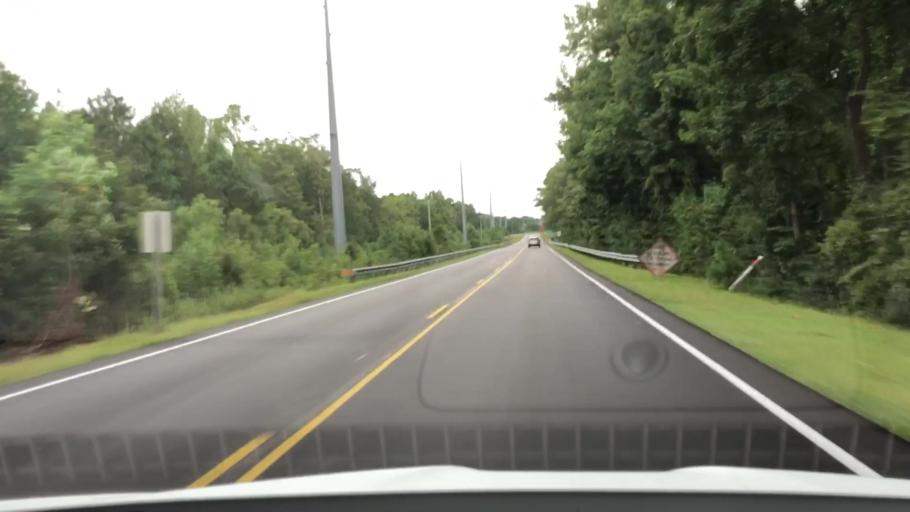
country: US
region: North Carolina
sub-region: Onslow County
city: Swansboro
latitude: 34.7966
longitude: -77.1316
